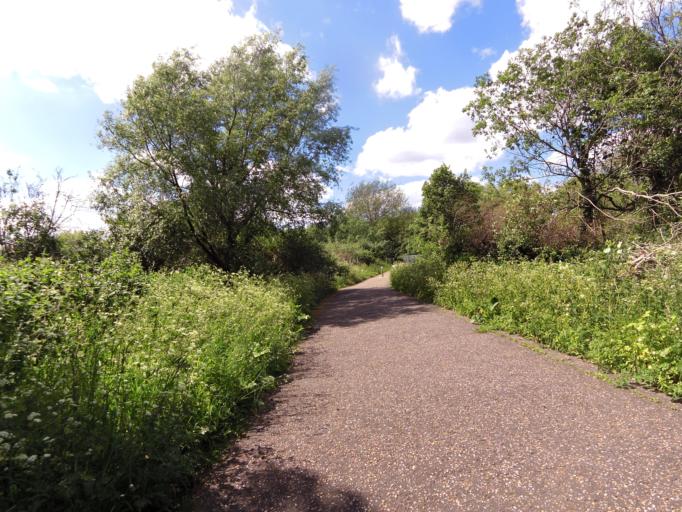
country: GB
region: England
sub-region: Norfolk
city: Norwich
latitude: 52.6412
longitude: 1.2823
